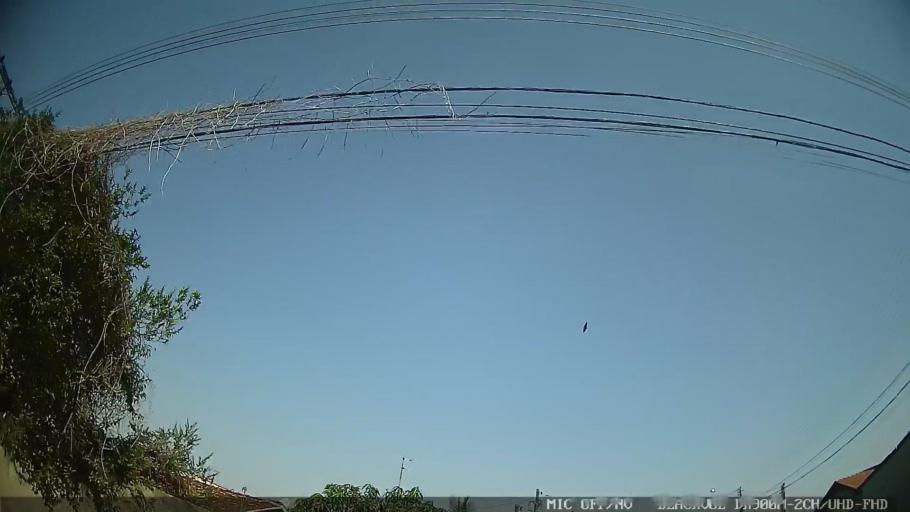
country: BR
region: Sao Paulo
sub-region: Itatiba
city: Itatiba
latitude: -22.9887
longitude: -46.8319
